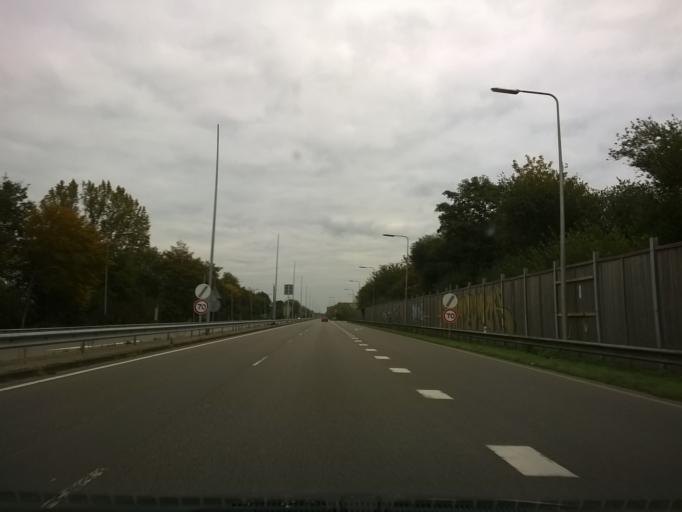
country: NL
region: Groningen
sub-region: Gemeente Groningen
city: Korrewegwijk
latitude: 53.2348
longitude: 6.5321
